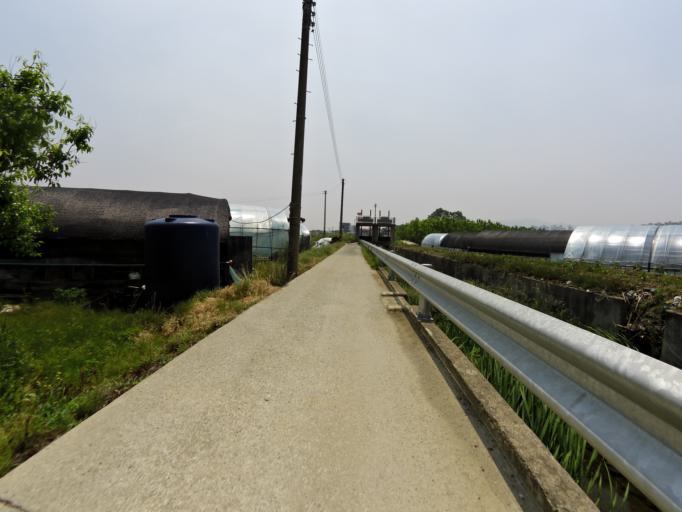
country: KR
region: Gyeongsangbuk-do
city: Gyeongsan-si
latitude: 35.8475
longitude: 128.7336
